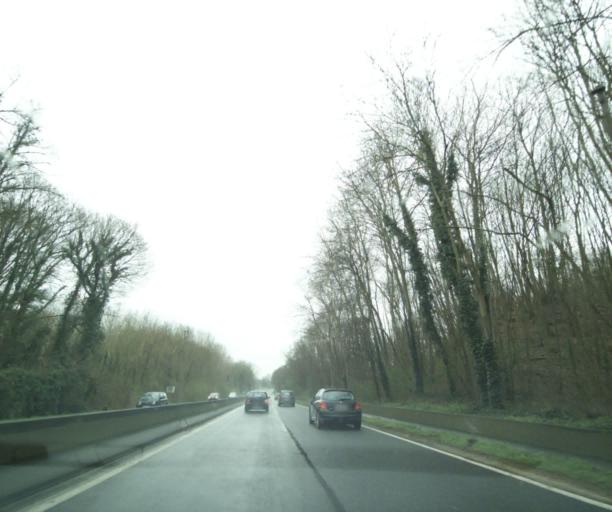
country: FR
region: Ile-de-France
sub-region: Departement de l'Essonne
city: Etrechy
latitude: 48.4789
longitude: 2.1914
